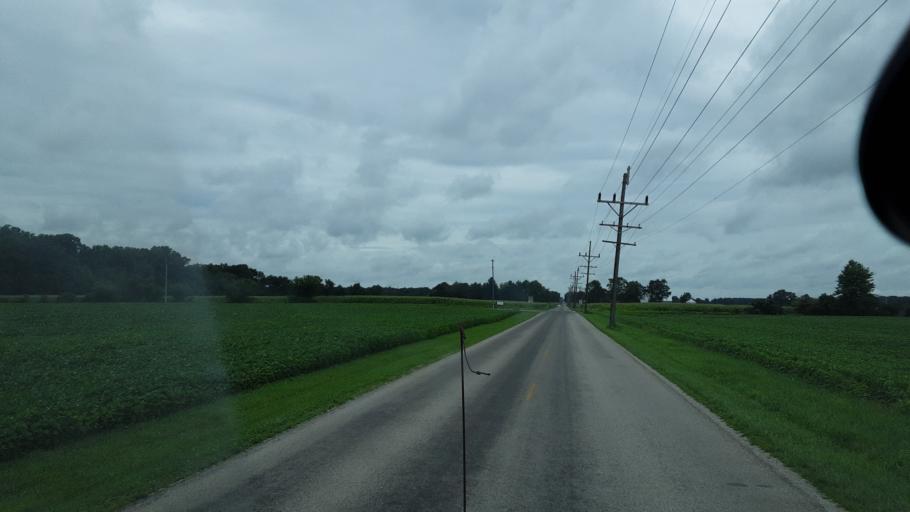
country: US
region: Indiana
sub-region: Jay County
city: Portland
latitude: 40.4446
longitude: -85.0199
